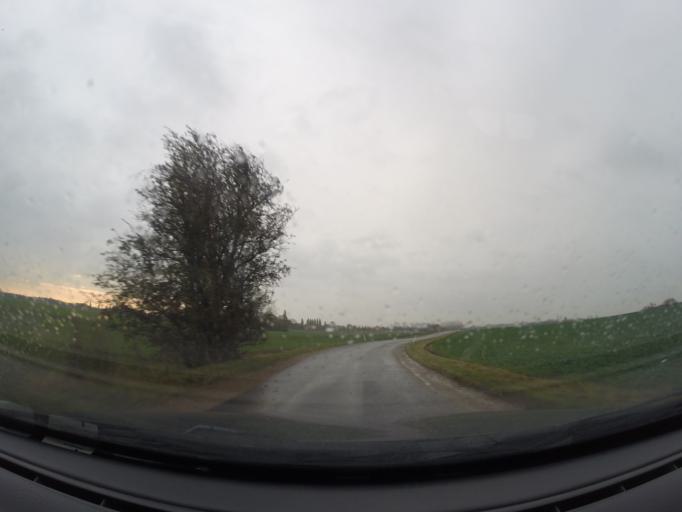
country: DK
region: Capital Region
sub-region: Hoje-Taastrup Kommune
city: Taastrup
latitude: 55.6760
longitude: 12.2766
